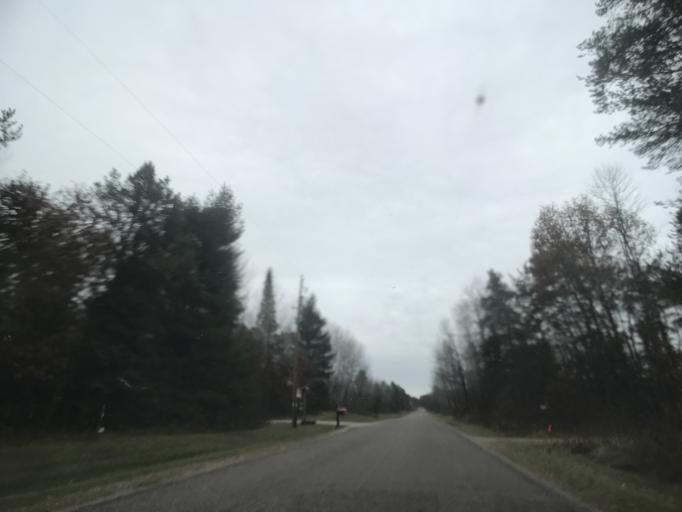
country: US
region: Wisconsin
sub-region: Oconto County
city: Gillett
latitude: 45.2777
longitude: -88.2571
